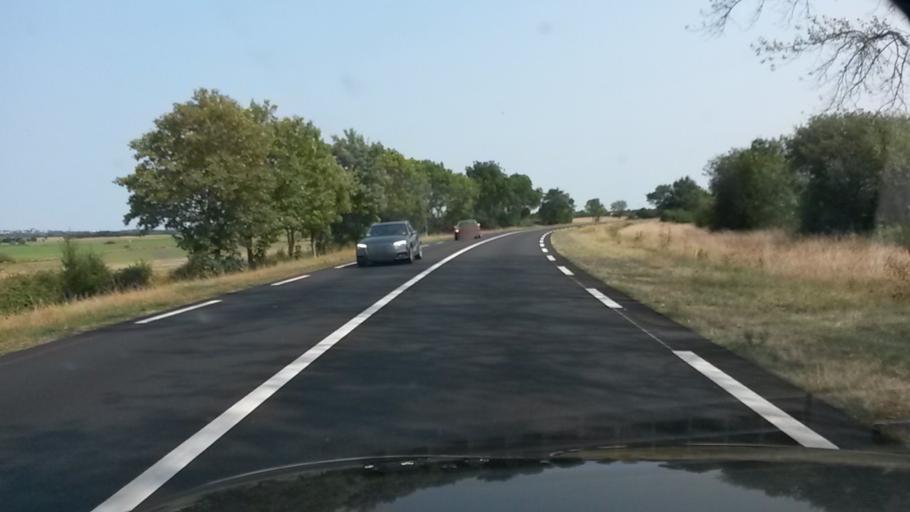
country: FR
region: Pays de la Loire
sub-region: Departement de la Loire-Atlantique
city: Ancenis
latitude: 47.3911
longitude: -1.1776
